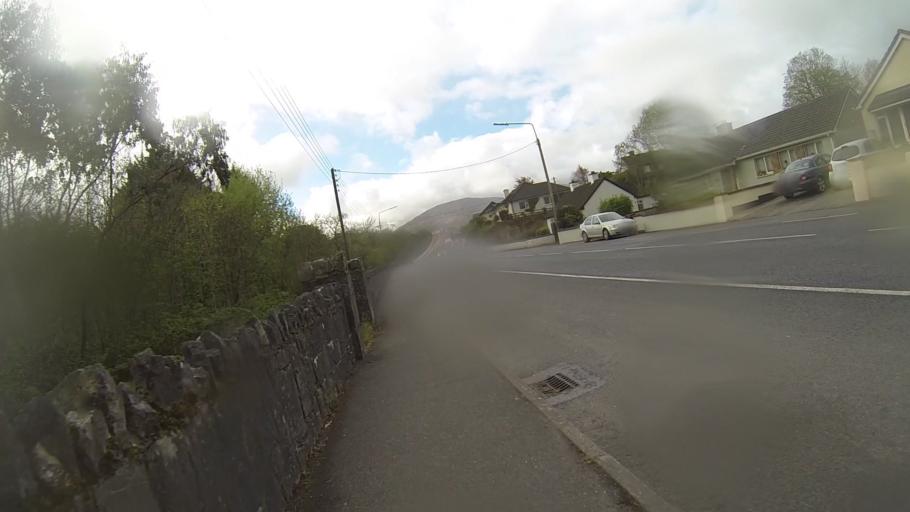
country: IE
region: Munster
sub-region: Ciarrai
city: Kenmare
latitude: 51.8828
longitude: -9.5853
